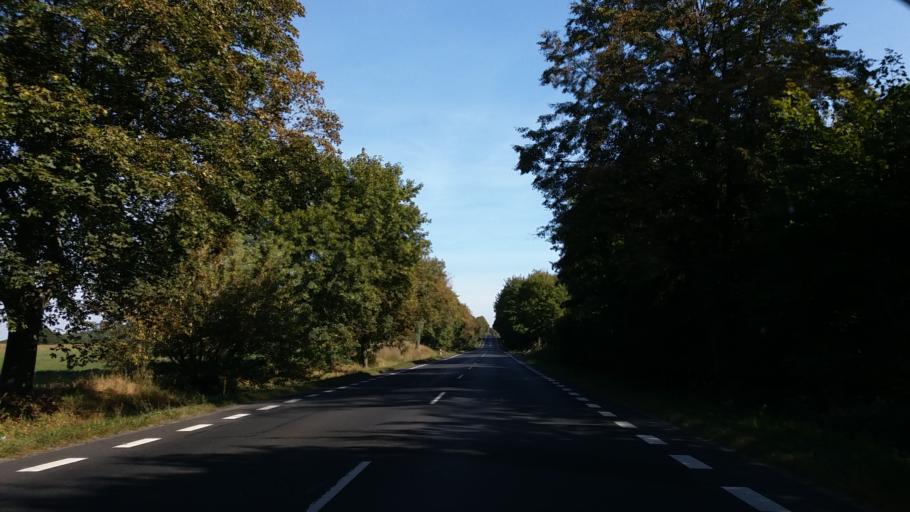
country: PL
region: Greater Poland Voivodeship
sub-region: Powiat miedzychodzki
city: Kwilcz
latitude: 52.5643
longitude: 16.0131
